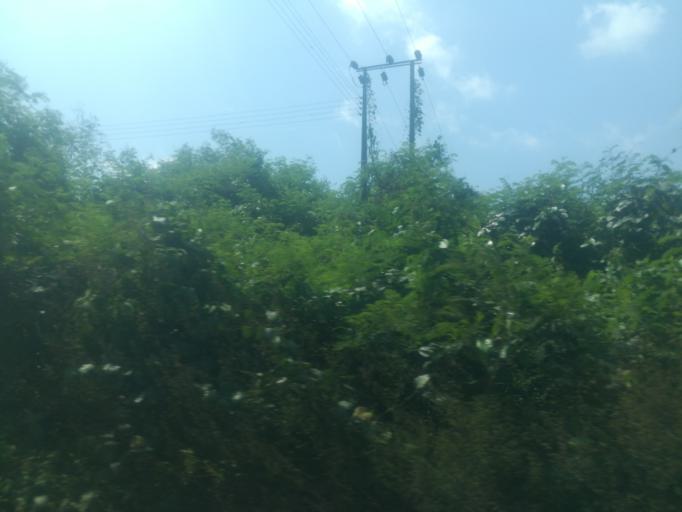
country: NG
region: Oyo
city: Moniya
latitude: 7.5729
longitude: 3.9145
